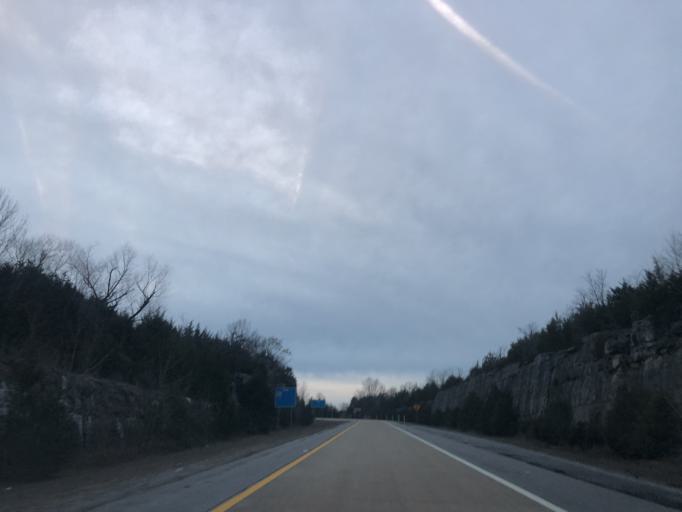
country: US
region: Tennessee
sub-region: Wilson County
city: Rural Hill
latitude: 36.1319
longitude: -86.3972
